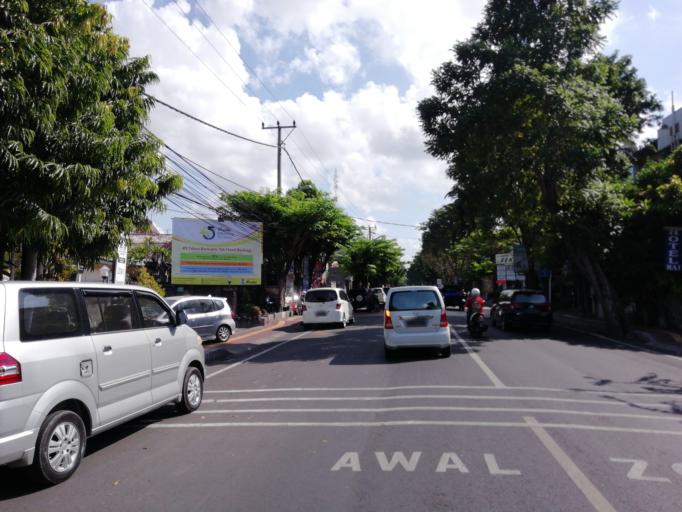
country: ID
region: Bali
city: Denpasar
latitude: -8.6721
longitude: 115.2155
